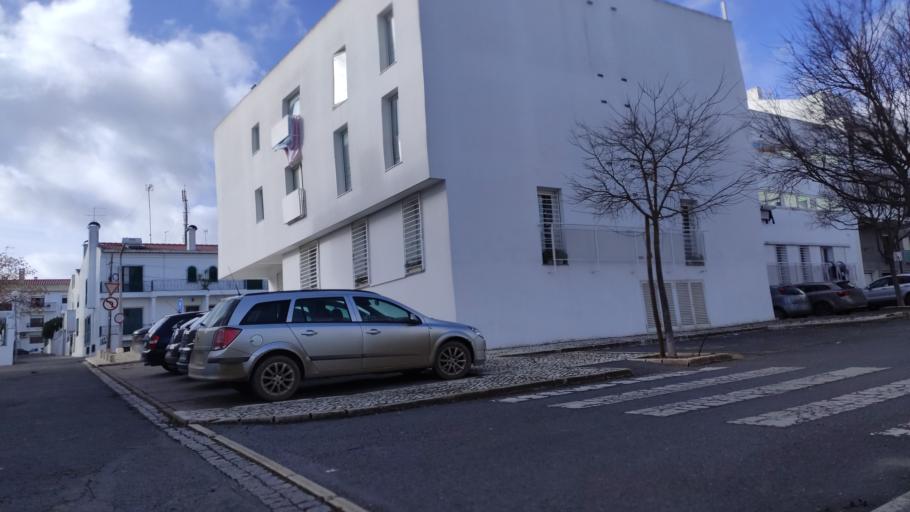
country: PT
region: Beja
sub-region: Beja
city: Beja
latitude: 38.0071
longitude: -7.8629
